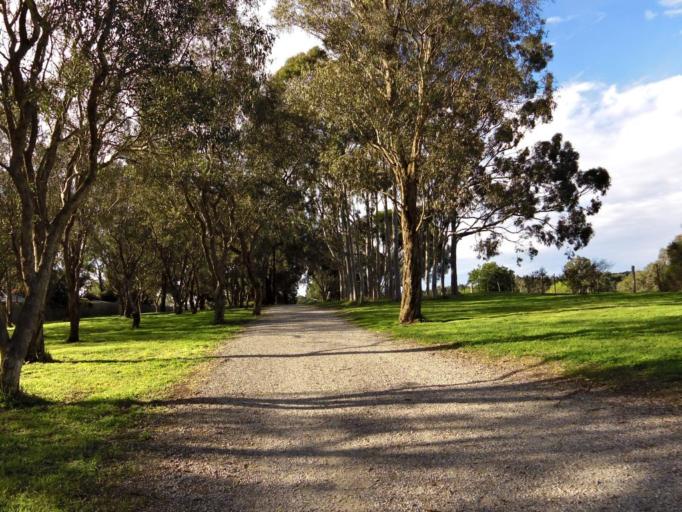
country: AU
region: Victoria
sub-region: Whitehorse
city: Vermont South
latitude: -37.8762
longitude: 145.1888
